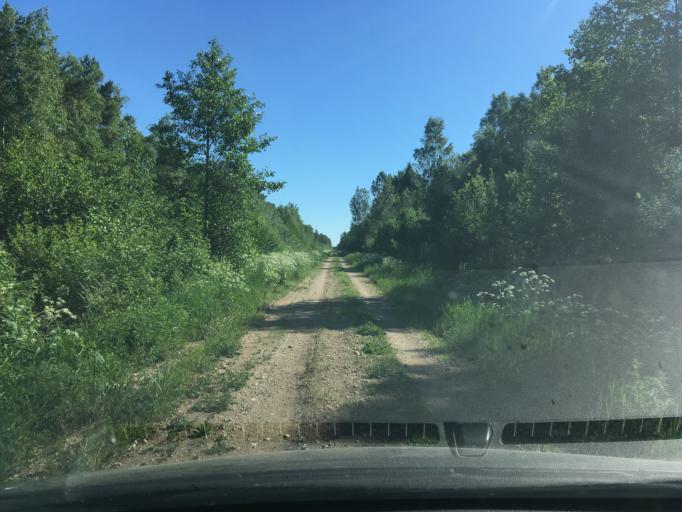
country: EE
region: Laeaene
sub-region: Lihula vald
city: Lihula
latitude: 58.6322
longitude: 23.7445
